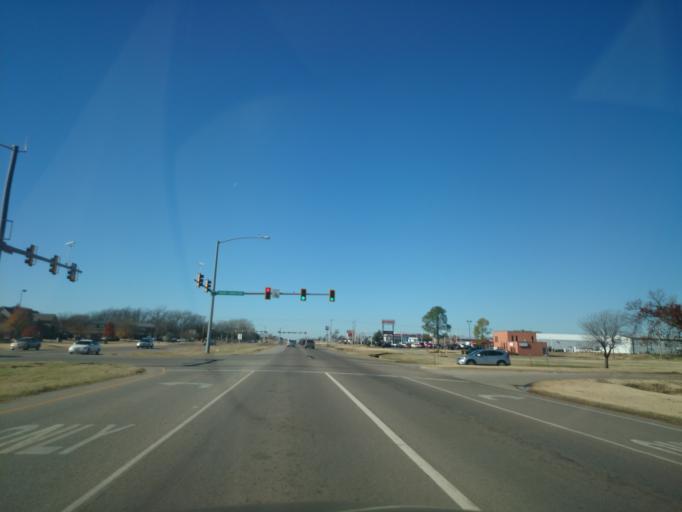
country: US
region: Oklahoma
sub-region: Payne County
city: Stillwater
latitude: 36.1161
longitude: -97.1195
